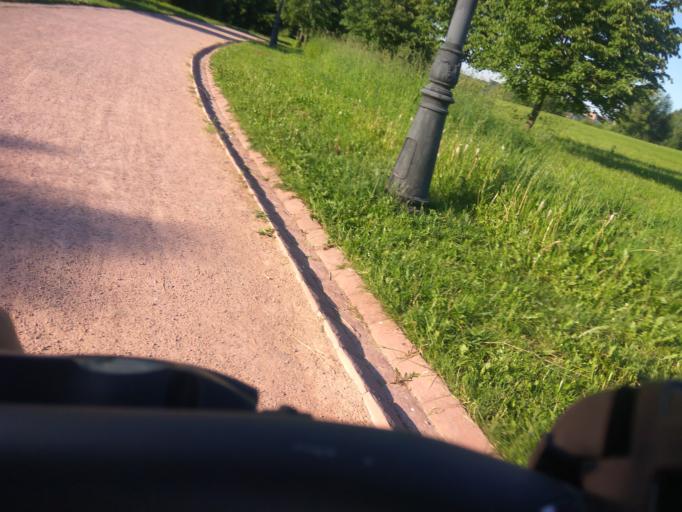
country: RU
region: Moscow
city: Orekhovo-Borisovo Severnoye
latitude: 55.6253
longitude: 37.6846
